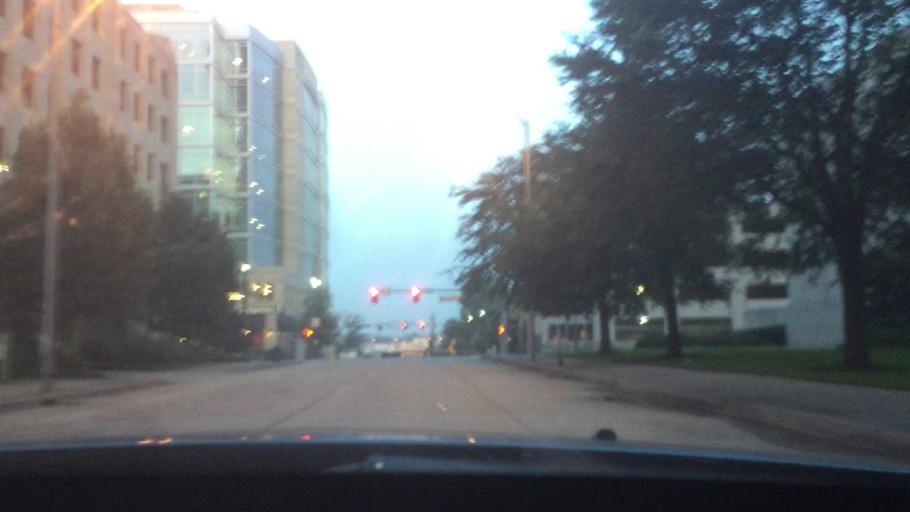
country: US
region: Louisiana
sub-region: West Baton Rouge Parish
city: Port Allen
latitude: 30.4525
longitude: -91.1888
